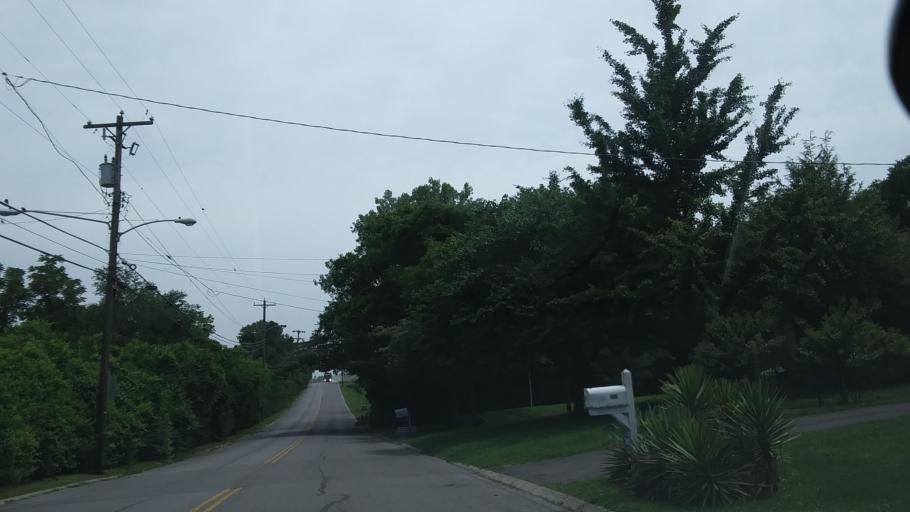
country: US
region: Tennessee
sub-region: Davidson County
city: Belle Meade
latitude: 36.1580
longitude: -86.8834
